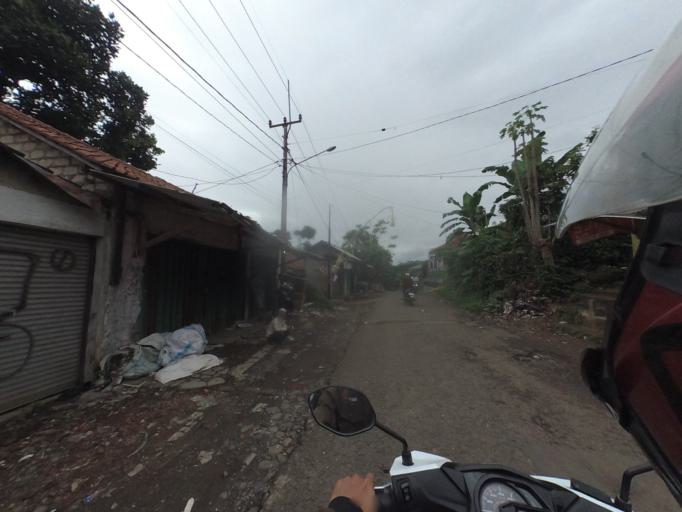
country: ID
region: West Java
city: Bogor
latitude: -6.6385
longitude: 106.7376
